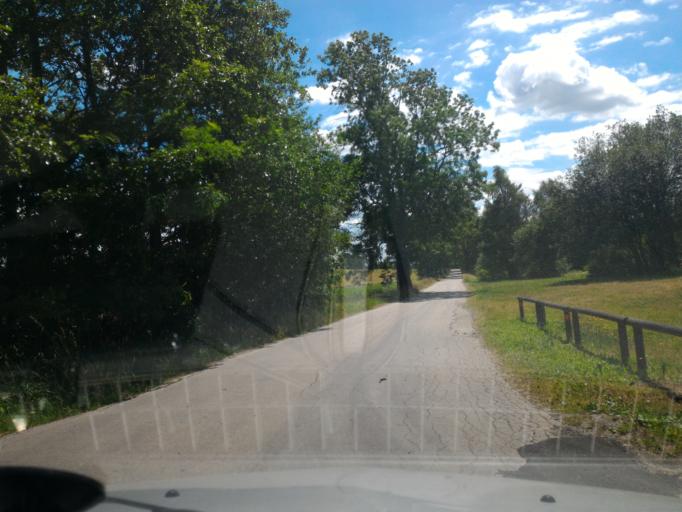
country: CZ
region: Vysocina
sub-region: Okres Jihlava
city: Telc
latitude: 49.2264
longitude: 15.3859
